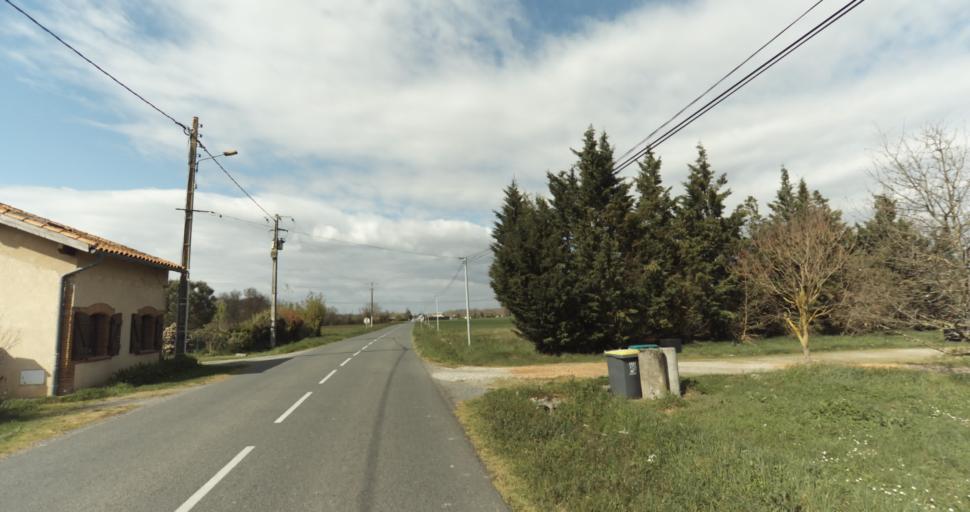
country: FR
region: Midi-Pyrenees
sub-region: Departement de la Haute-Garonne
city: Auterive
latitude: 43.3833
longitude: 1.4600
